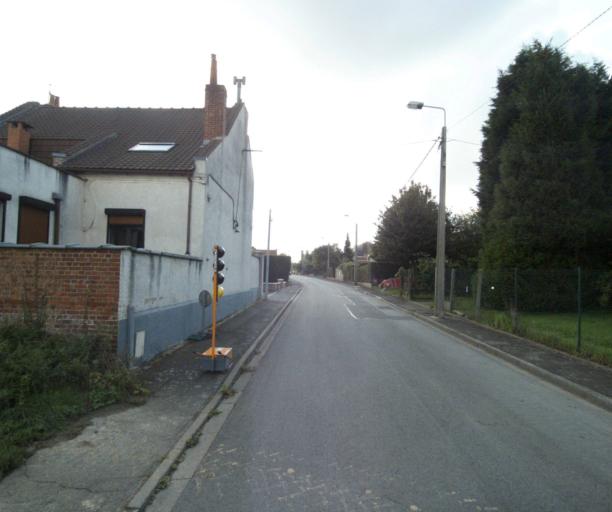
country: FR
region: Nord-Pas-de-Calais
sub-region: Departement du Nord
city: Perenchies
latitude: 50.6727
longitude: 2.9756
